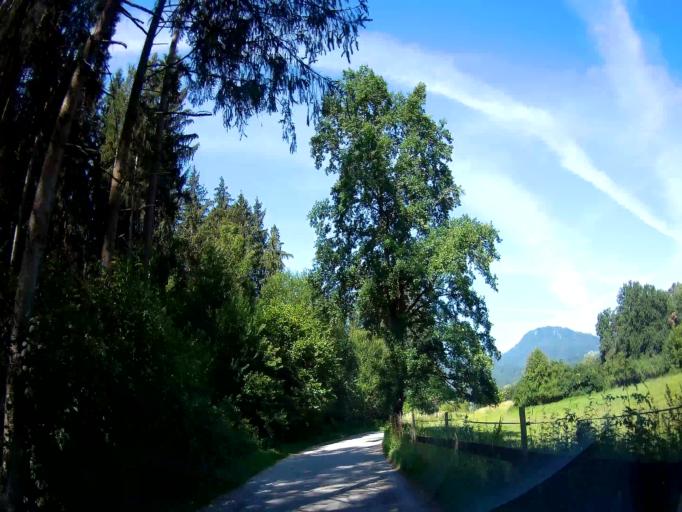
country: AT
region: Carinthia
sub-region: Politischer Bezirk Klagenfurt Land
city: Maria Saal
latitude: 46.6893
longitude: 14.3540
